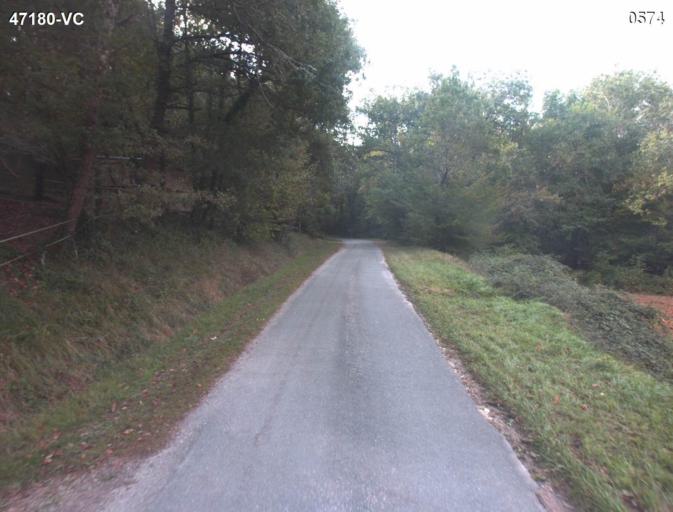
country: FR
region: Aquitaine
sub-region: Departement du Lot-et-Garonne
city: Sainte-Colombe-en-Bruilhois
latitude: 44.1845
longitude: 0.4393
